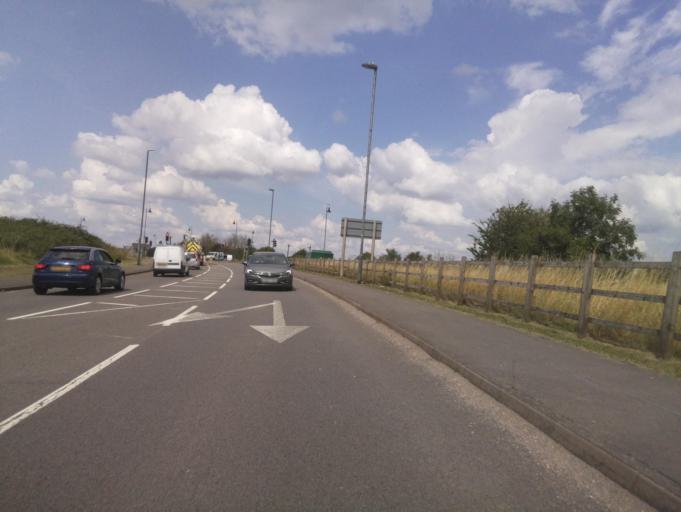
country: GB
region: England
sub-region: Borough of Swindon
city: Wroughton
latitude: 51.5430
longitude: -1.8018
